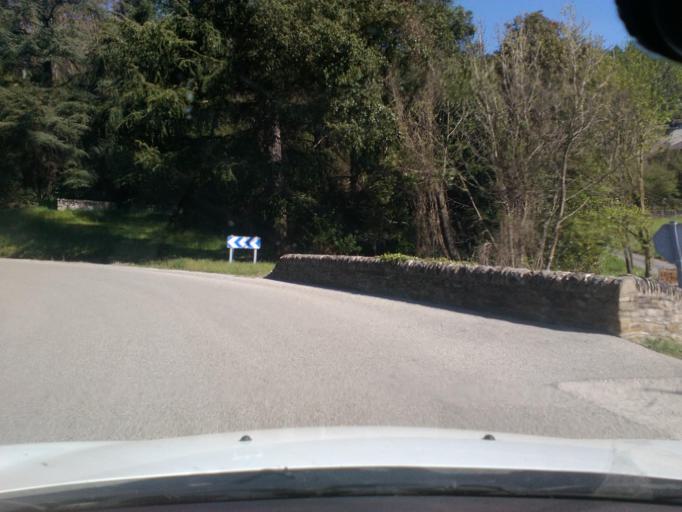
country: FR
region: Languedoc-Roussillon
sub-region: Departement du Gard
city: Saint-Jean-du-Gard
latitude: 44.1709
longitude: 3.7632
